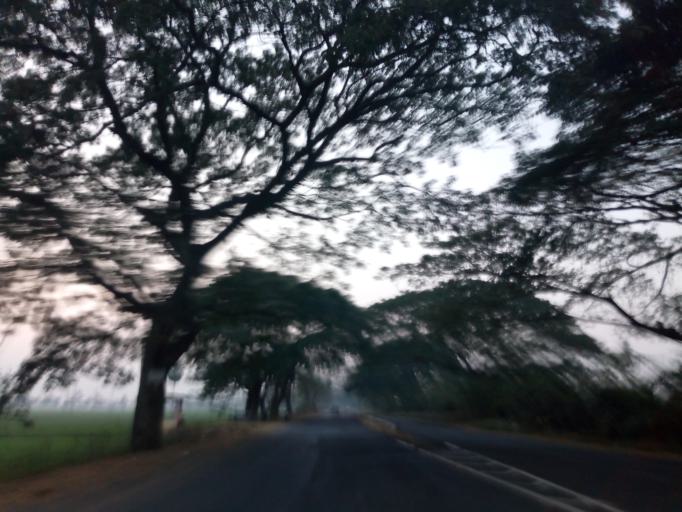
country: IN
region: Andhra Pradesh
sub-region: West Godavari
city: Tadepallegudem
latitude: 16.8203
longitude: 81.4819
